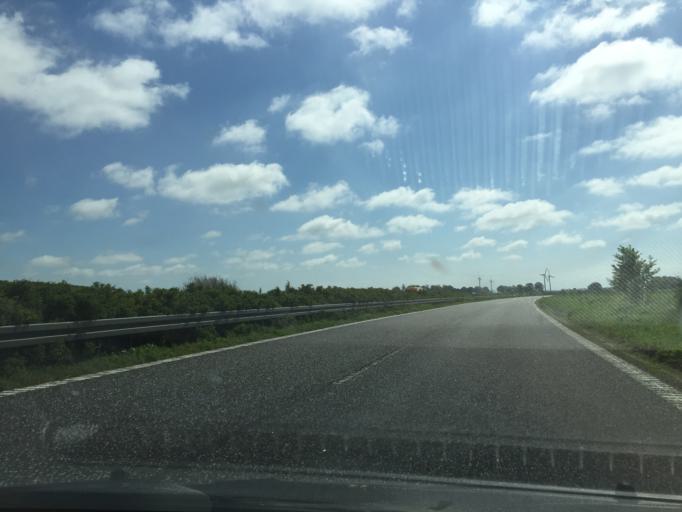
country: DK
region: Zealand
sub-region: Lolland Kommune
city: Holeby
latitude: 54.7516
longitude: 11.4596
